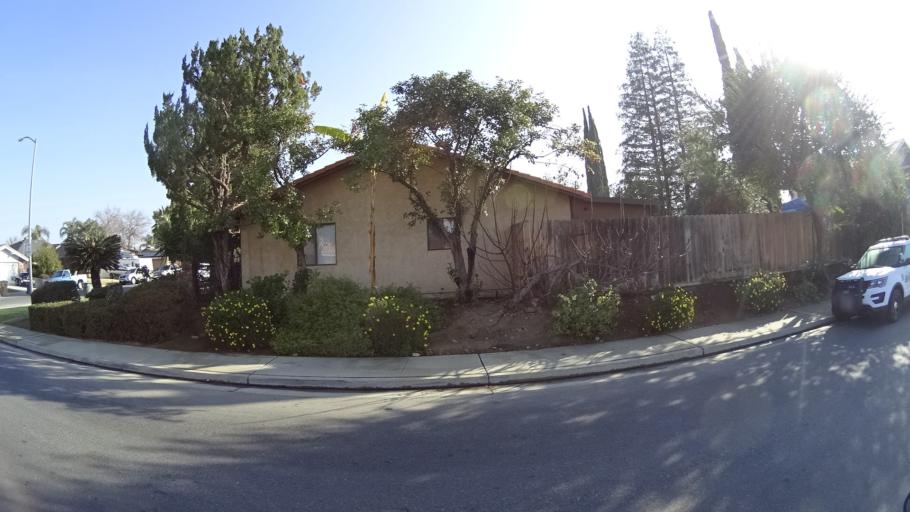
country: US
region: California
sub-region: Kern County
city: Oildale
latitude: 35.4035
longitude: -118.9290
